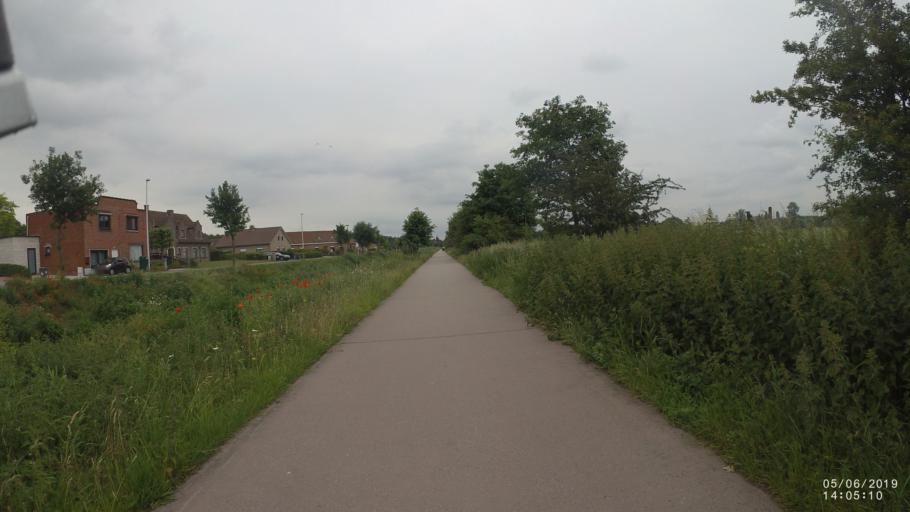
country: BE
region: Flanders
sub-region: Provincie Oost-Vlaanderen
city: Wachtebeke
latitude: 51.1790
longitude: 3.8509
